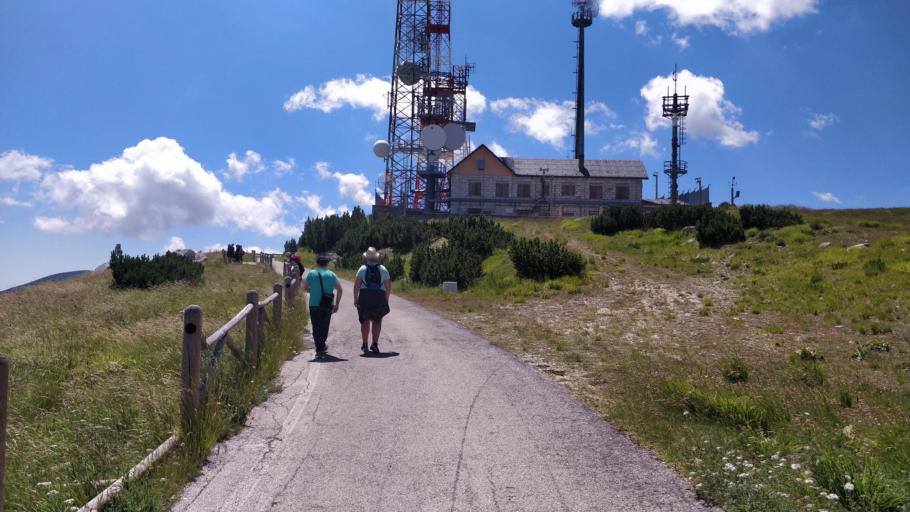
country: IT
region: Abruzzo
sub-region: Provincia di Chieti
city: Pretoro
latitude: 42.1597
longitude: 14.1328
